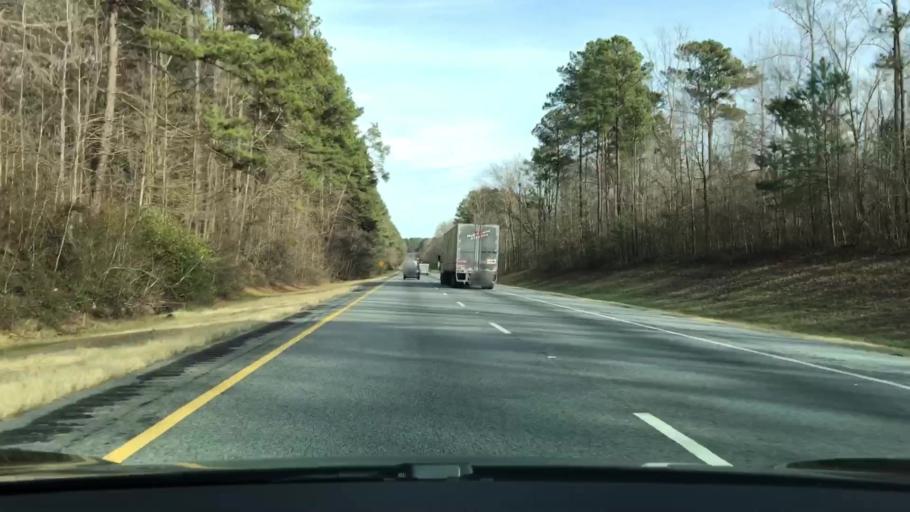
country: US
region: Georgia
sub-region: Morgan County
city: Madison
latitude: 33.5763
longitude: -83.5558
